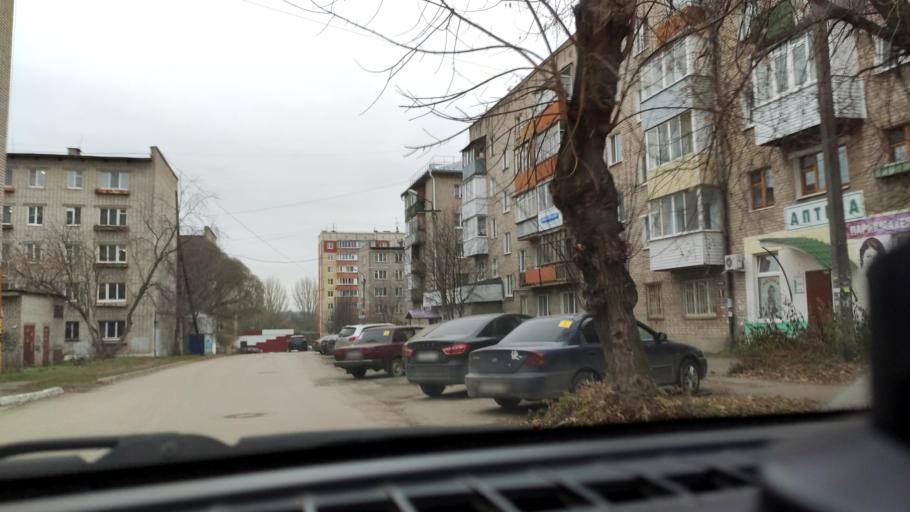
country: RU
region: Perm
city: Perm
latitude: 58.0211
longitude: 56.2986
